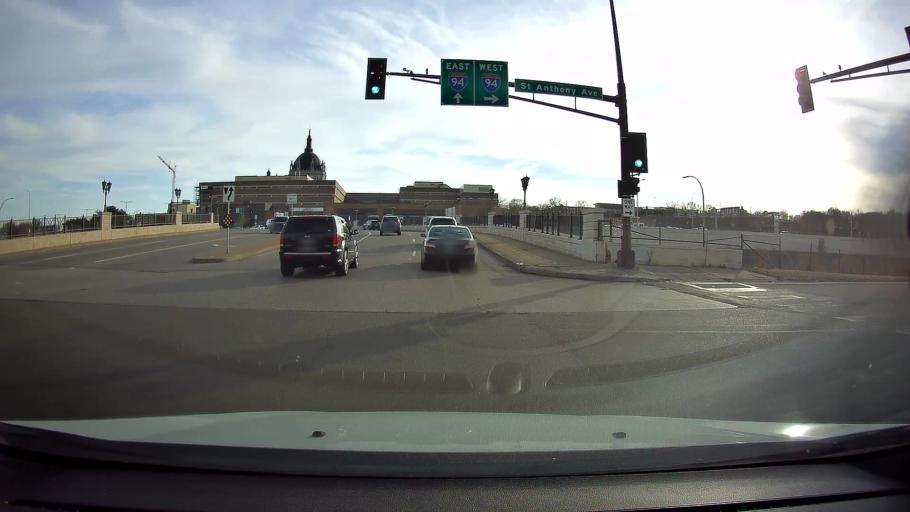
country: US
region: Minnesota
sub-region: Ramsey County
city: Saint Paul
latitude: 44.9515
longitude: -93.1100
